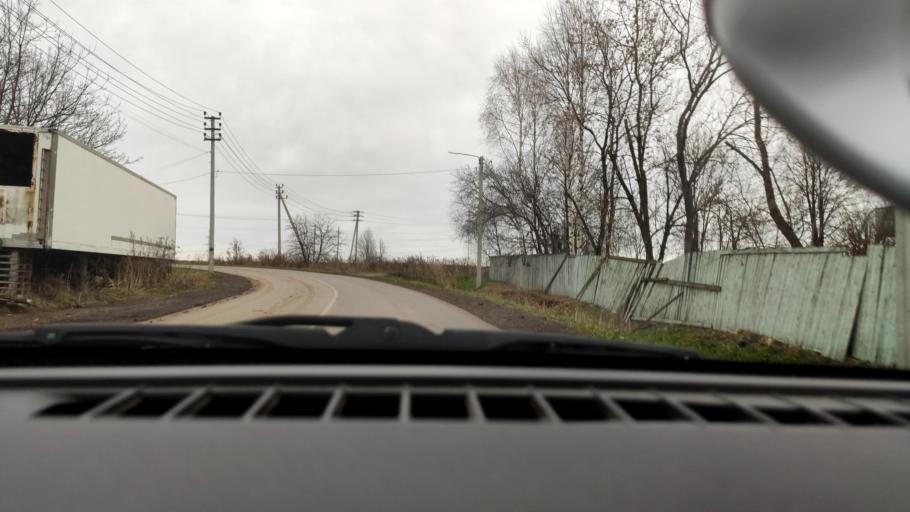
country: RU
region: Perm
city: Ferma
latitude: 57.9180
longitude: 56.3317
